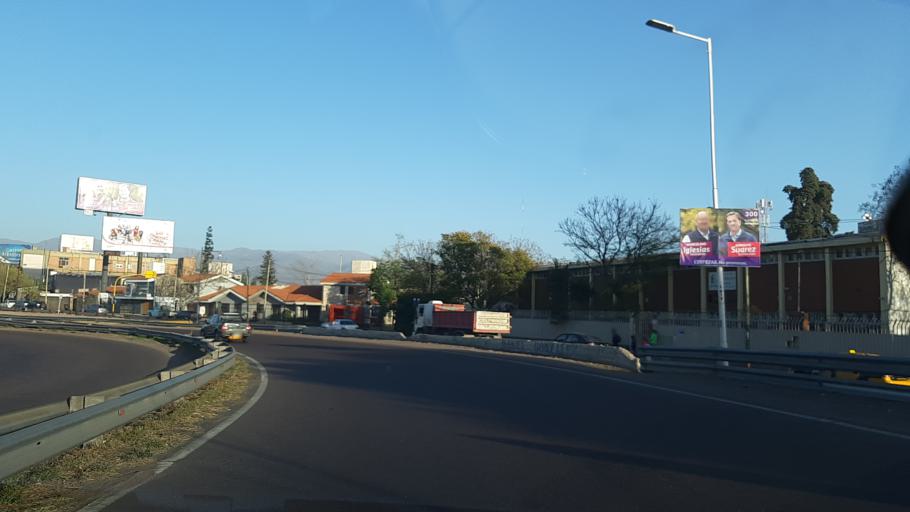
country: AR
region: Mendoza
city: Mendoza
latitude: -32.8967
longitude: -68.8192
